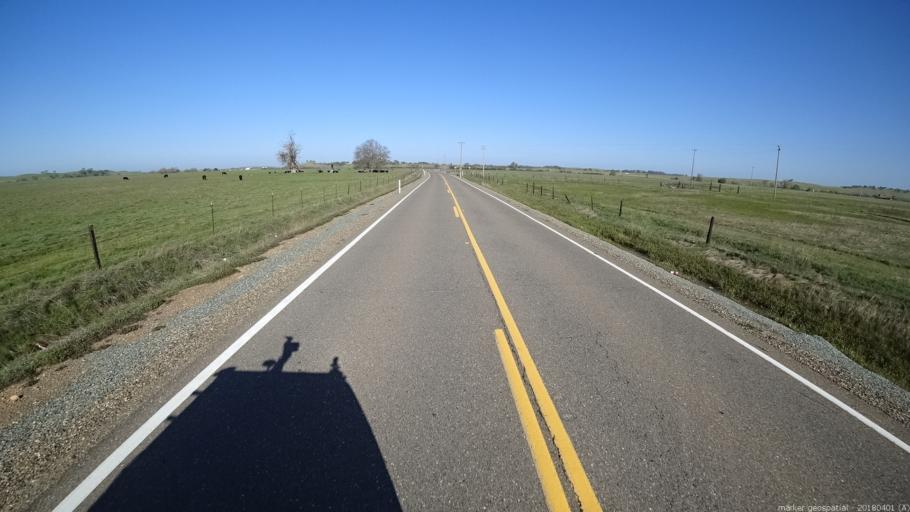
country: US
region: California
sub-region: Sacramento County
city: Rancho Murieta
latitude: 38.4197
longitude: -121.0438
